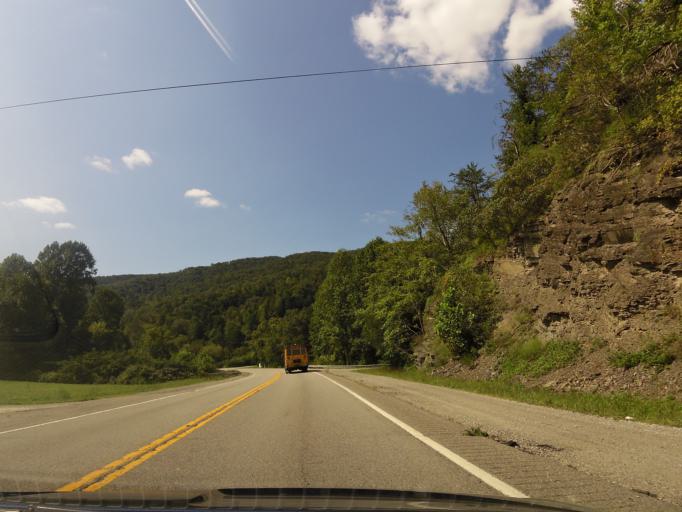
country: US
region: Kentucky
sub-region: Harlan County
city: Loyall
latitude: 36.8309
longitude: -83.4581
